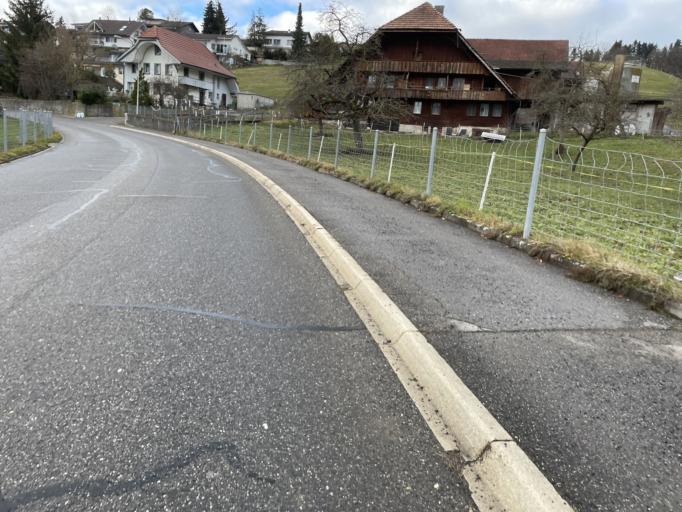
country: CH
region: Bern
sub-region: Thun District
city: Heimberg
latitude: 46.7961
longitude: 7.6000
